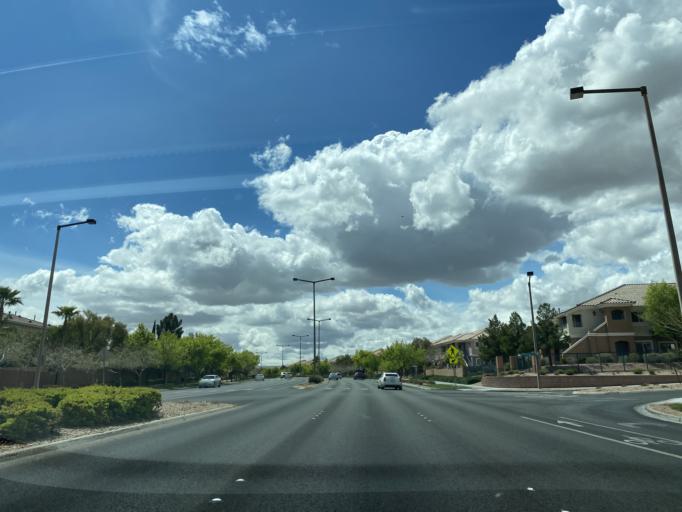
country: US
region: Nevada
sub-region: Clark County
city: Summerlin South
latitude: 36.1723
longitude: -115.3243
